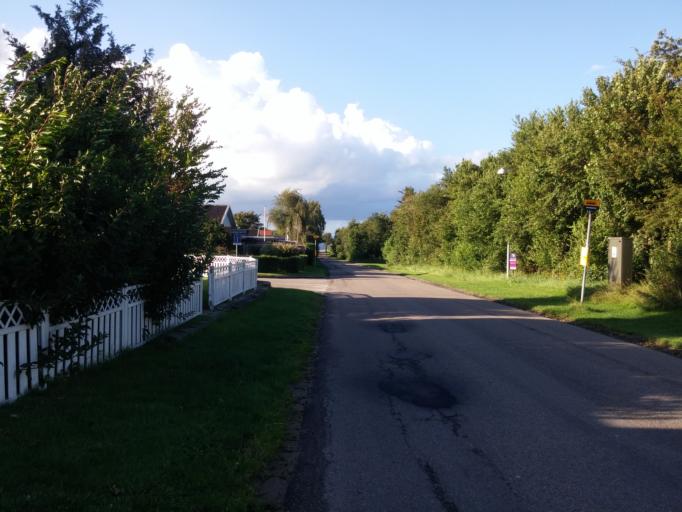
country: DK
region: Zealand
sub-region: Kalundborg Kommune
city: Svebolle
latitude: 55.7514
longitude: 11.3386
